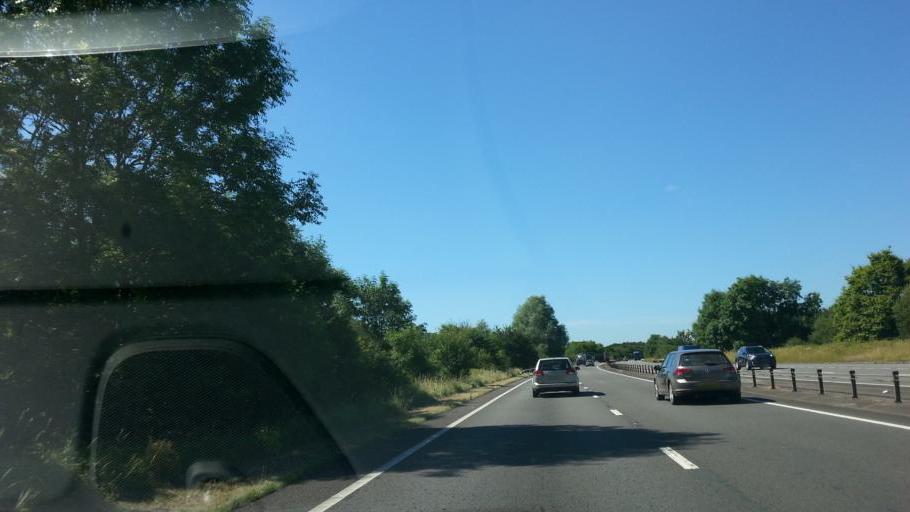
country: GB
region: Wales
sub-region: Monmouthshire
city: Llangwm
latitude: 51.7142
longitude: -2.8623
